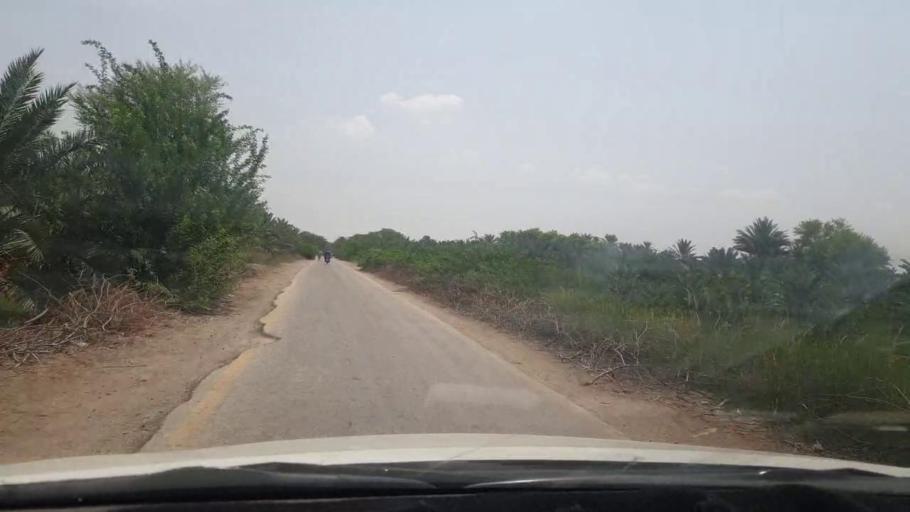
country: PK
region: Sindh
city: Khairpur
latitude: 27.5334
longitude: 68.8943
